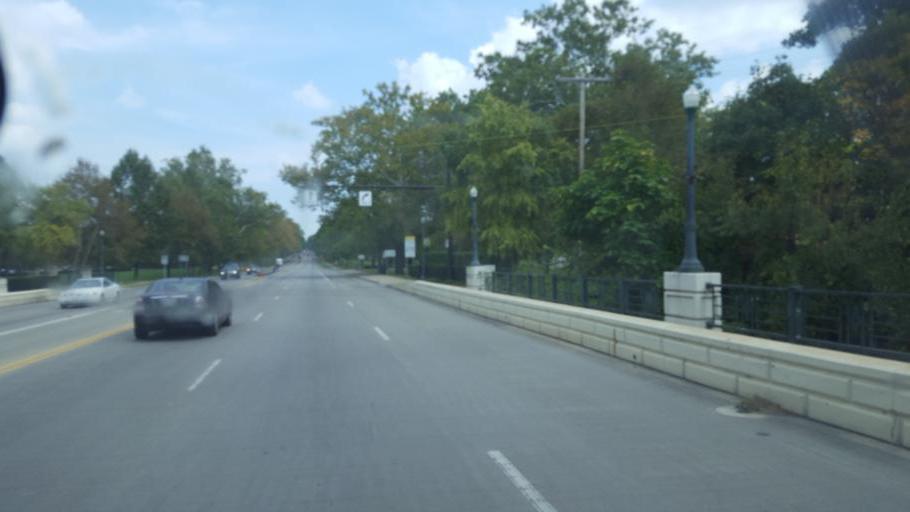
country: US
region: Ohio
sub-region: Franklin County
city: Bexley
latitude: 39.9679
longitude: -82.9500
